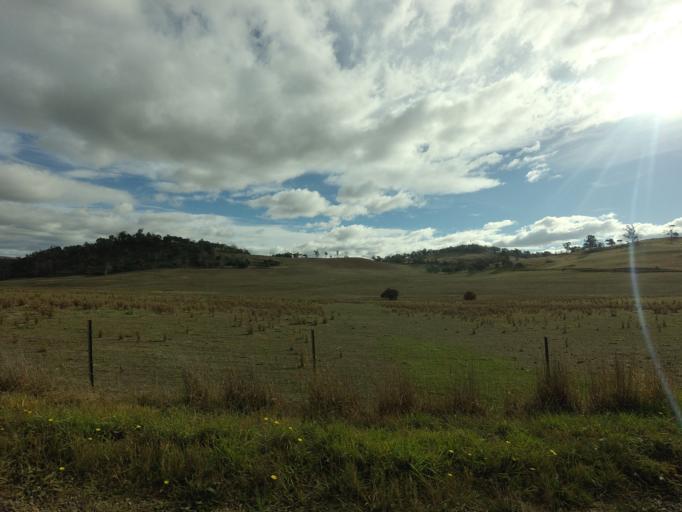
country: AU
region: Tasmania
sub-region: Brighton
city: Bridgewater
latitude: -42.4632
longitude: 147.2776
